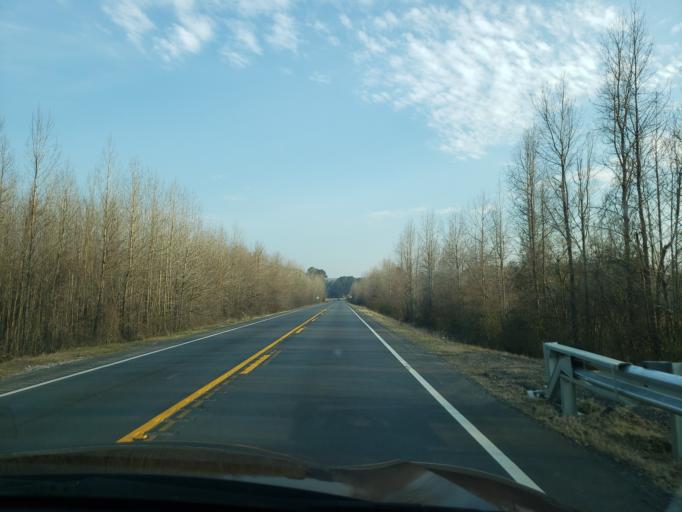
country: US
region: Alabama
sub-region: Hale County
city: Greensboro
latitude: 32.8289
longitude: -87.6040
